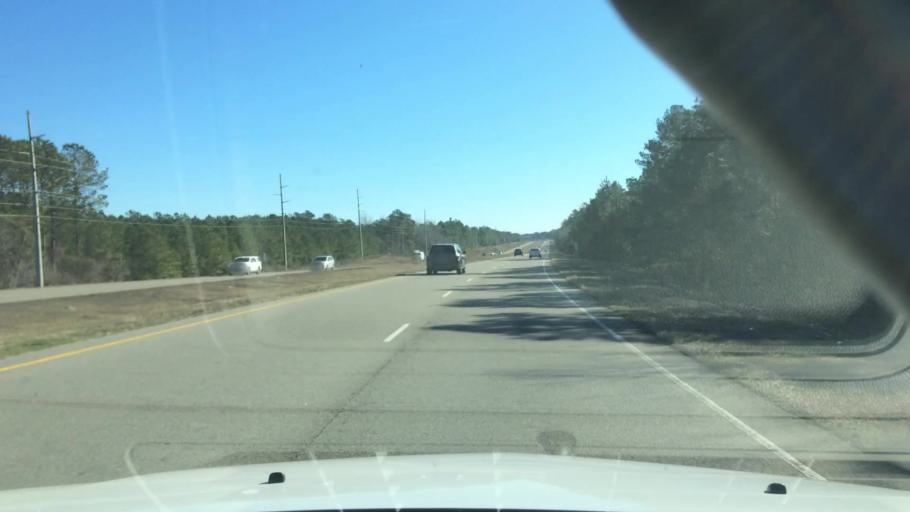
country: US
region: North Carolina
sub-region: Brunswick County
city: Shallotte
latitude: 33.9892
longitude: -78.3831
